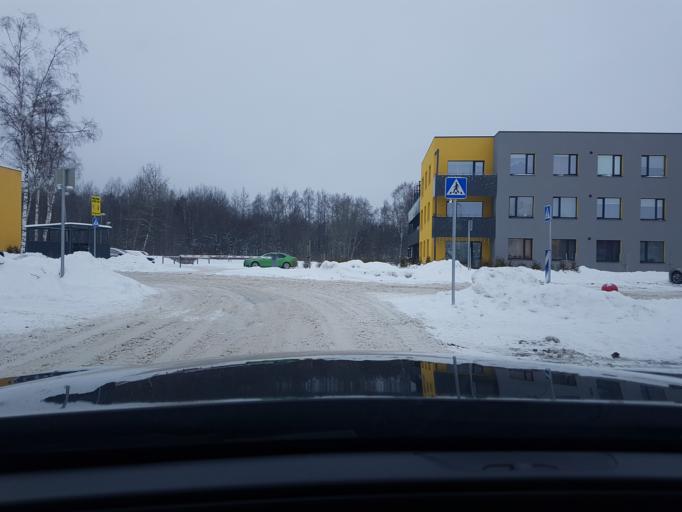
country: EE
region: Harju
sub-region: Saue vald
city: Laagri
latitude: 59.3523
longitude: 24.6392
